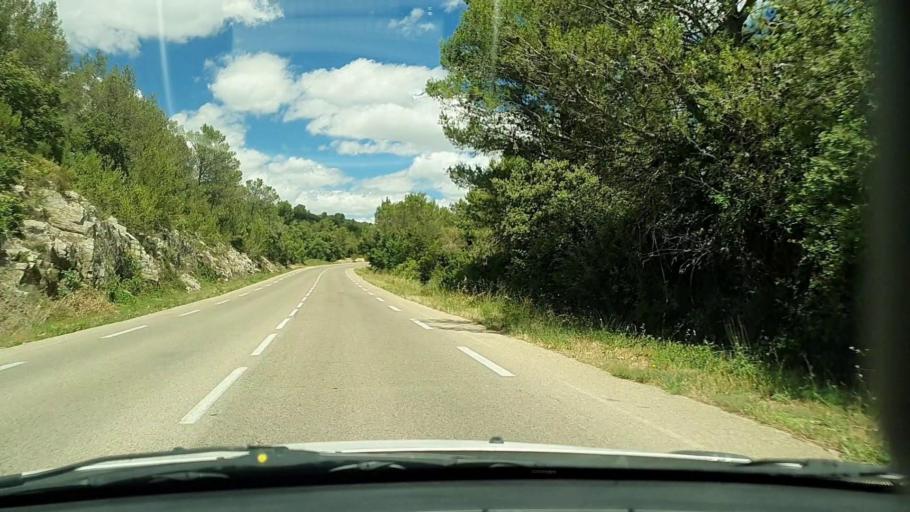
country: FR
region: Languedoc-Roussillon
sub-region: Departement du Gard
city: Poulx
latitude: 43.8822
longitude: 4.4172
